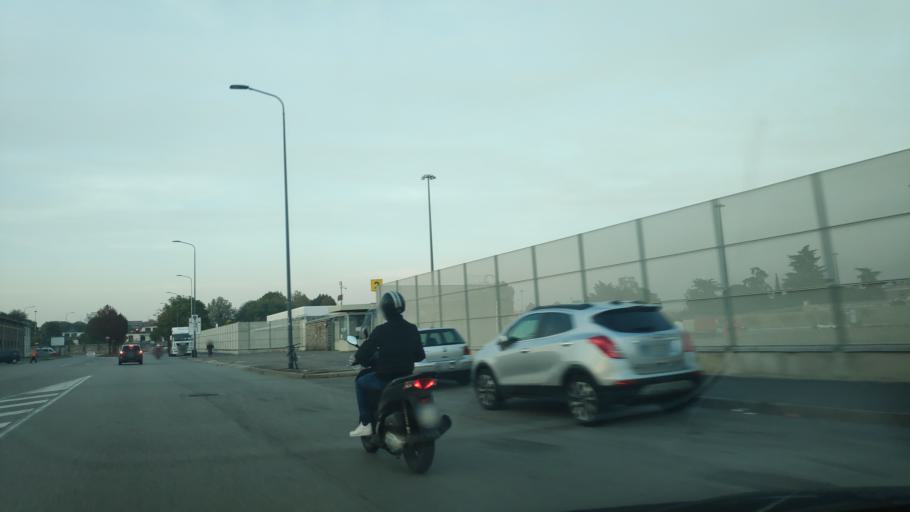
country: IT
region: Lombardy
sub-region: Citta metropolitana di Milano
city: Chiaravalle
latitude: 45.4541
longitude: 9.2294
